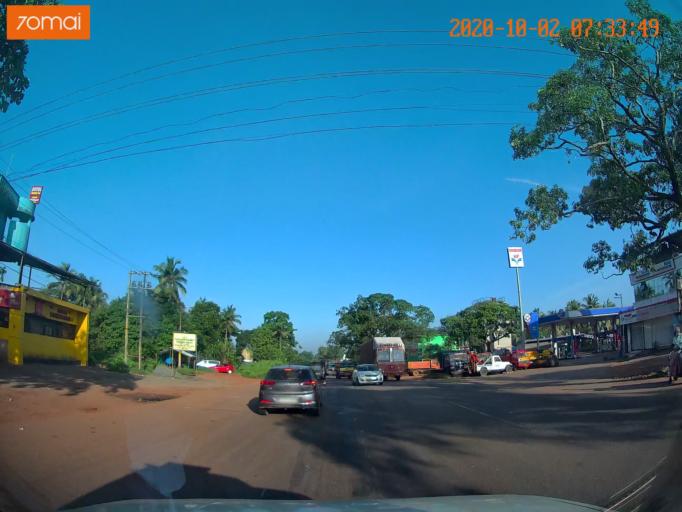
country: IN
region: Kerala
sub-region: Malappuram
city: Pariyapuram
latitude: 11.0613
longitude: 75.9350
